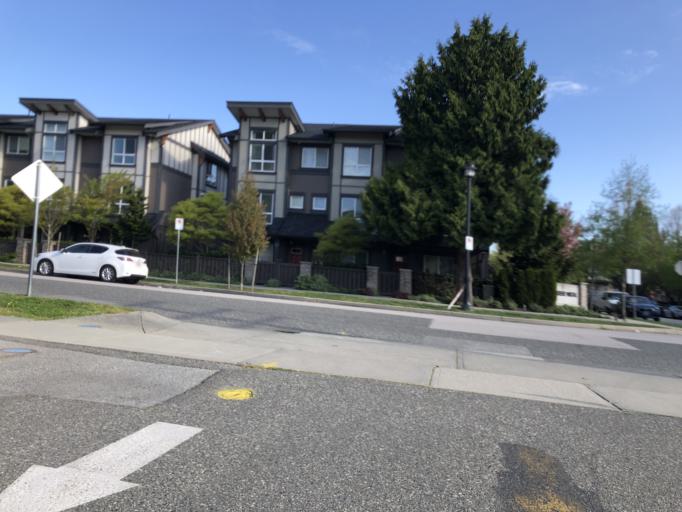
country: CA
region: British Columbia
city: Richmond
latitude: 49.1655
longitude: -123.1196
